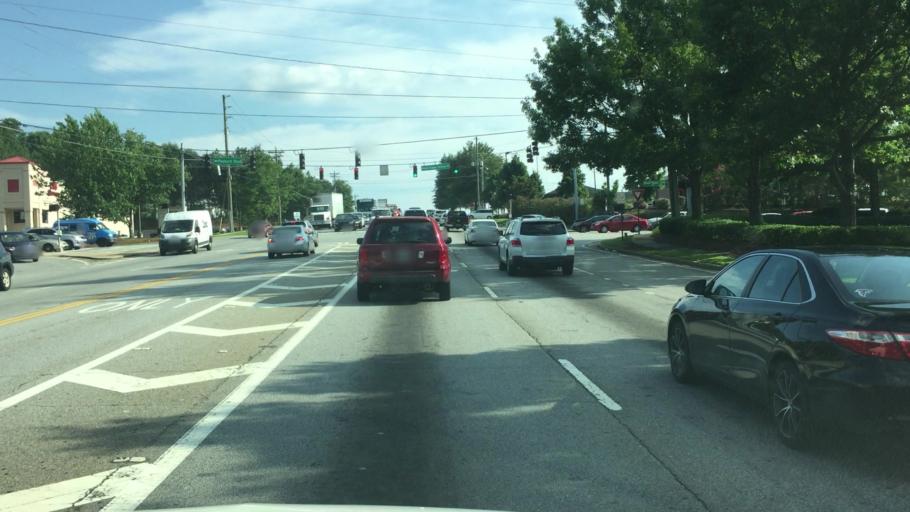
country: US
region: Georgia
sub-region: Gwinnett County
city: Snellville
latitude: 33.8734
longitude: -84.0142
